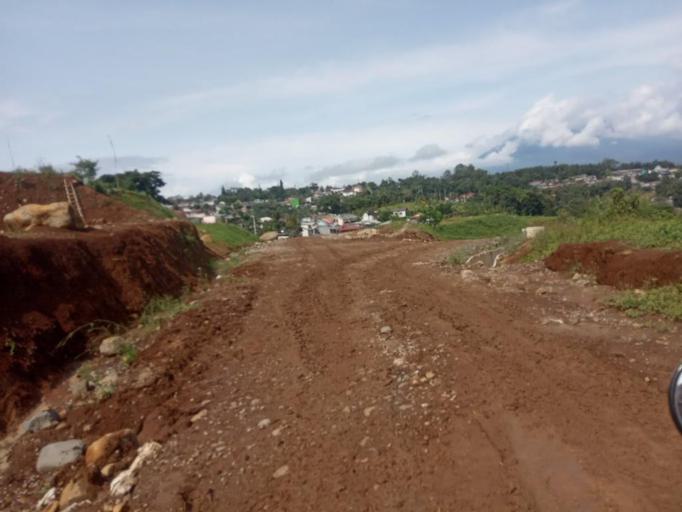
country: ID
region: West Java
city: Caringin
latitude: -6.6603
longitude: 106.8801
